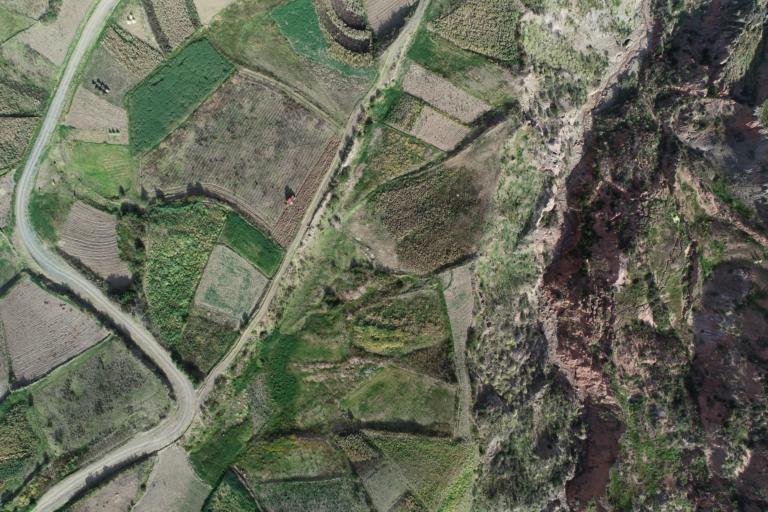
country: BO
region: La Paz
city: La Paz
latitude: -16.5540
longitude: -67.9909
